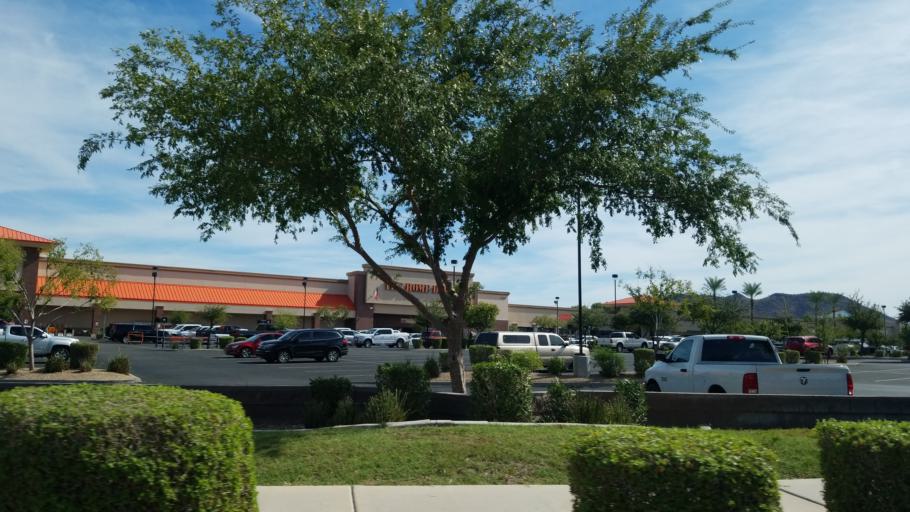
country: US
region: Arizona
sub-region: Maricopa County
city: Peoria
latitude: 33.6659
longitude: -112.1909
